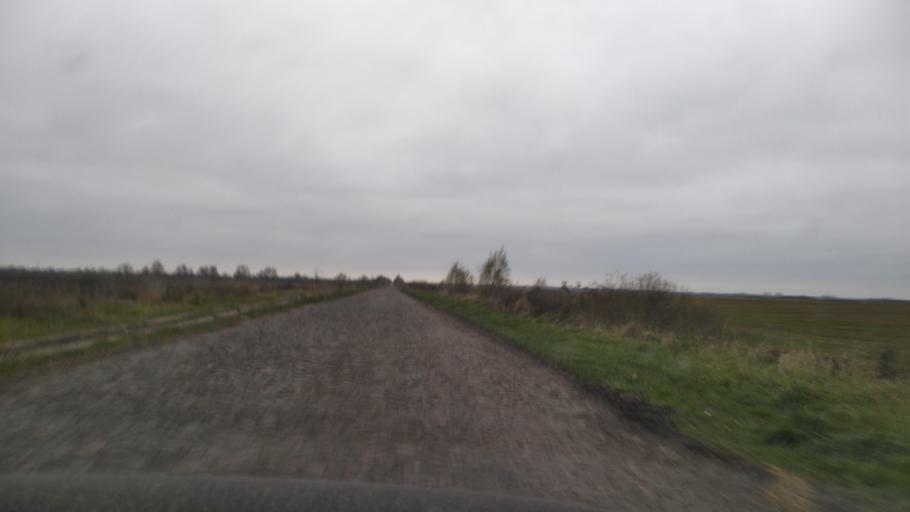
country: BY
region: Brest
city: Davyd-Haradok
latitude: 52.0094
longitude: 27.2055
